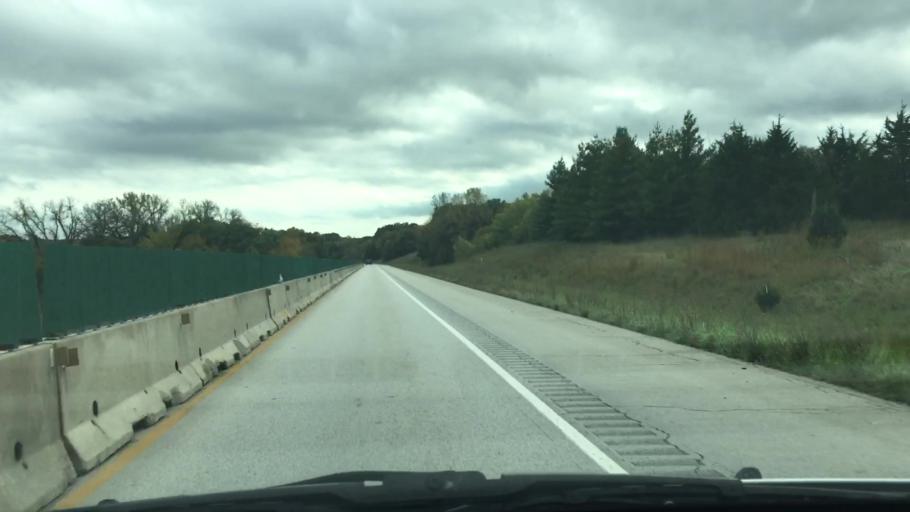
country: US
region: Iowa
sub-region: Decatur County
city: Leon
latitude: 40.7198
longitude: -93.8444
